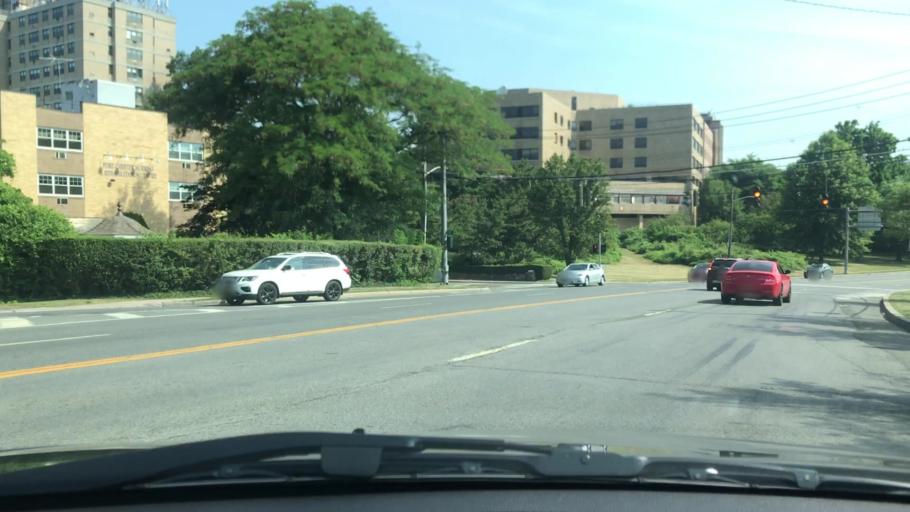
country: US
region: New York
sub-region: Westchester County
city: Rye
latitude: 40.9925
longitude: -73.6766
